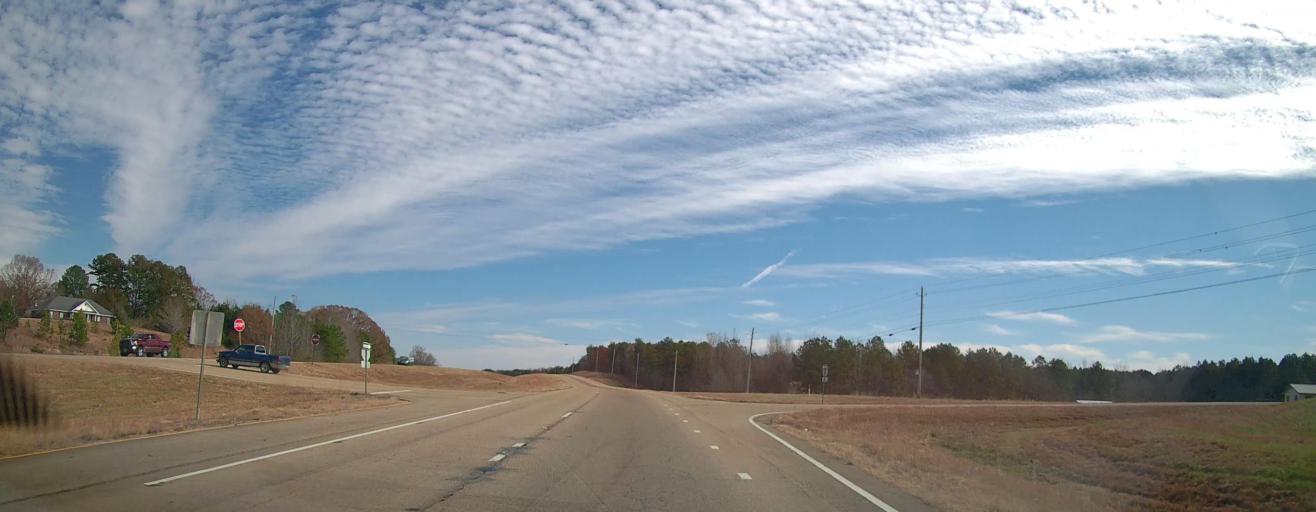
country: US
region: Mississippi
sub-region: Alcorn County
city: Corinth
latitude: 34.9316
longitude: -88.7169
